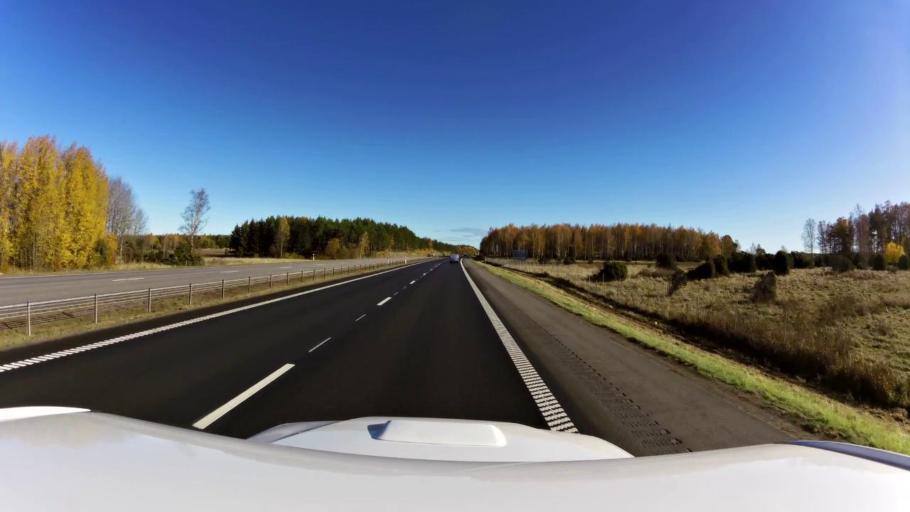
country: SE
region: OEstergoetland
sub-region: Linkopings Kommun
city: Vikingstad
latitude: 58.3840
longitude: 15.3673
